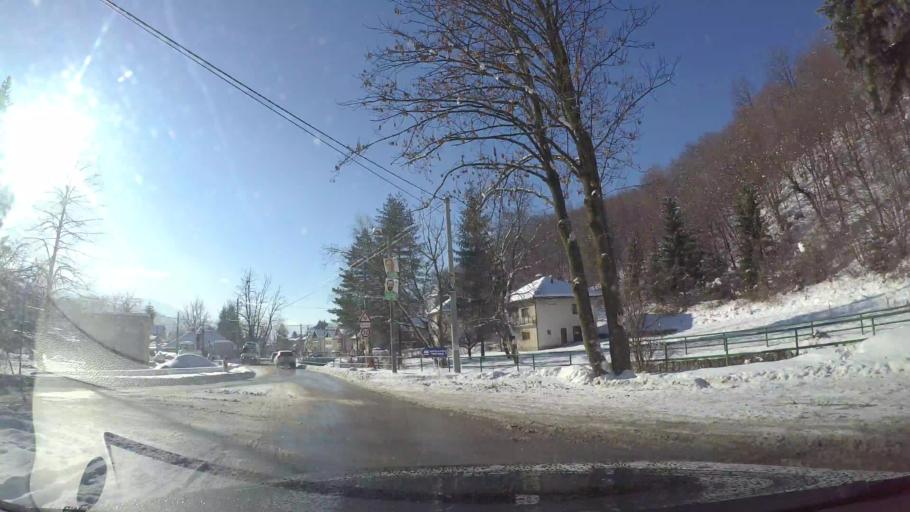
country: BA
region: Federation of Bosnia and Herzegovina
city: Kobilja Glava
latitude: 43.8874
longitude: 18.4161
